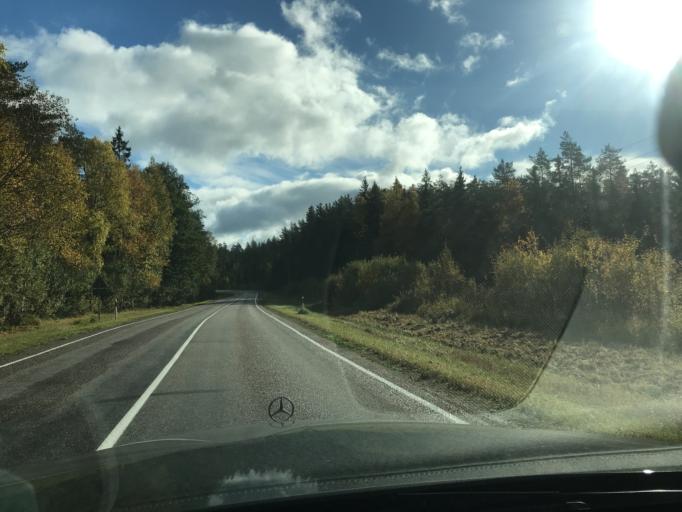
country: EE
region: Valgamaa
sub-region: Torva linn
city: Torva
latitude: 58.0099
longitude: 26.1401
